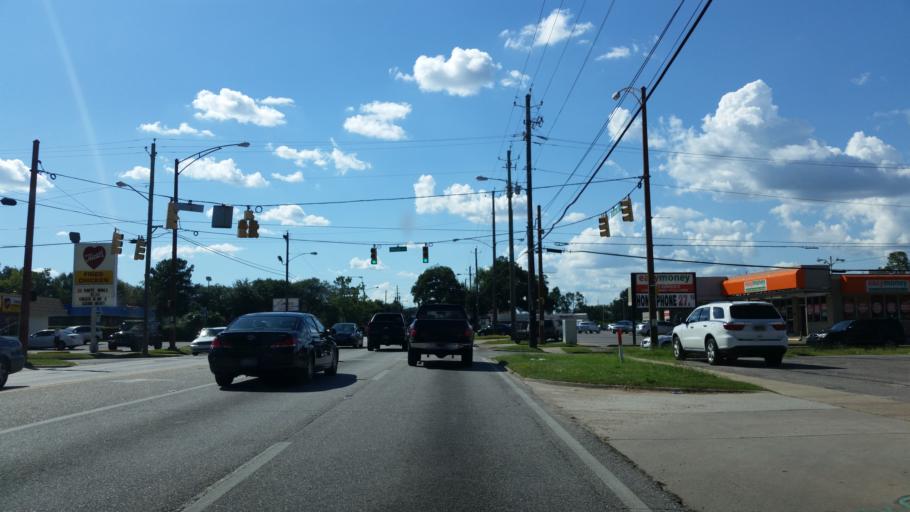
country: US
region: Alabama
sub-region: Mobile County
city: Prichard
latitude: 30.6992
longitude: -88.1097
